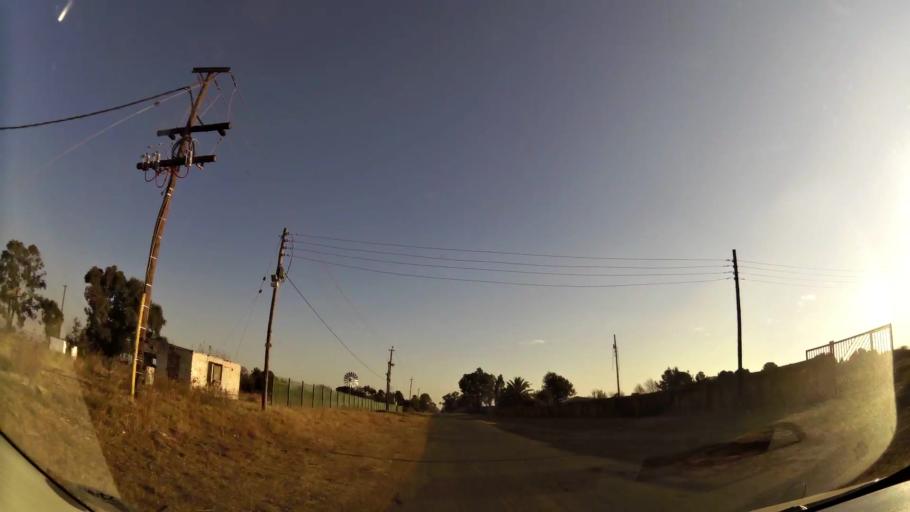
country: ZA
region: Gauteng
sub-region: West Rand District Municipality
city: Randfontein
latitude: -26.2134
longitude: 27.6572
